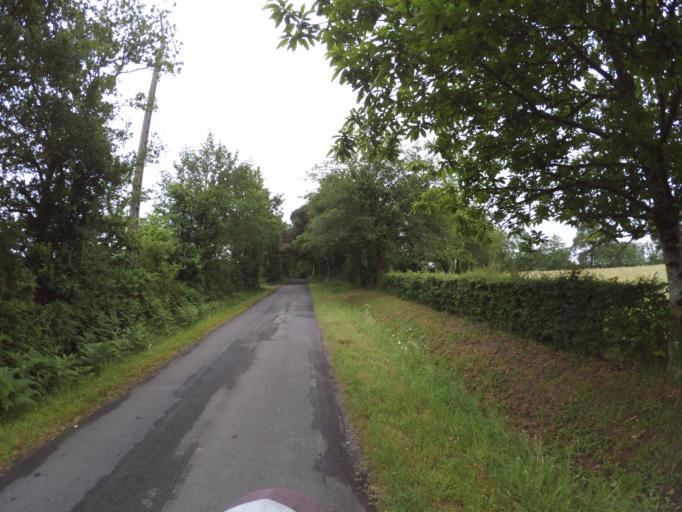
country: FR
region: Pays de la Loire
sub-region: Departement de la Vendee
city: La Roche-sur-Yon
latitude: 46.6327
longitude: -1.4265
